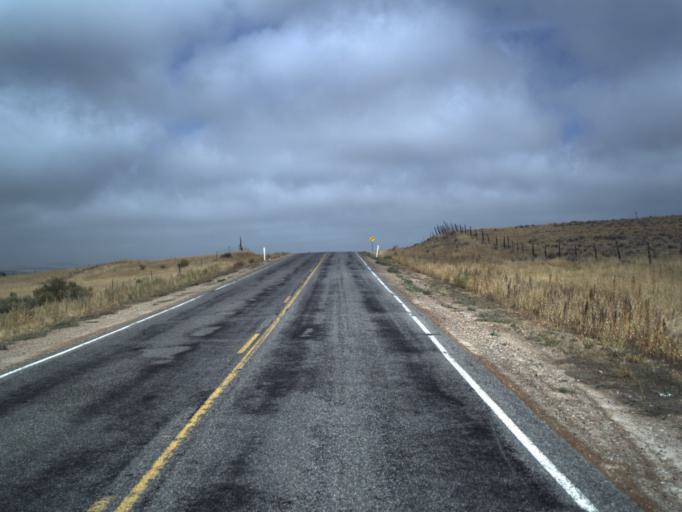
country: US
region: Utah
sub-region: Rich County
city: Randolph
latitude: 41.4769
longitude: -111.1126
